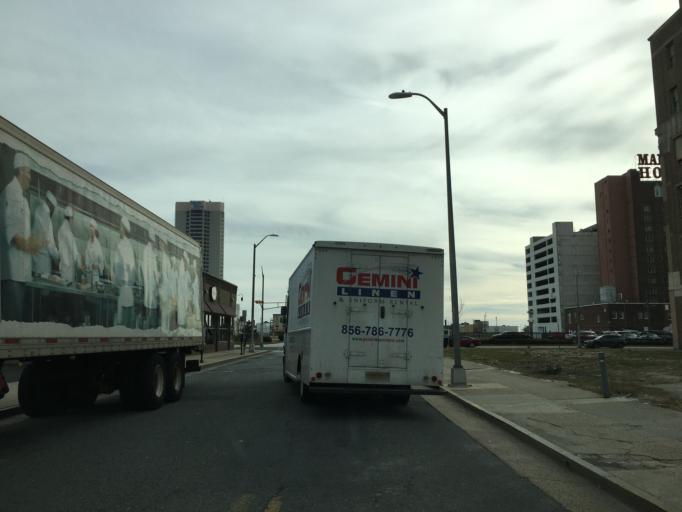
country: US
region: New Jersey
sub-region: Atlantic County
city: Atlantic City
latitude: 39.3601
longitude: -74.4299
